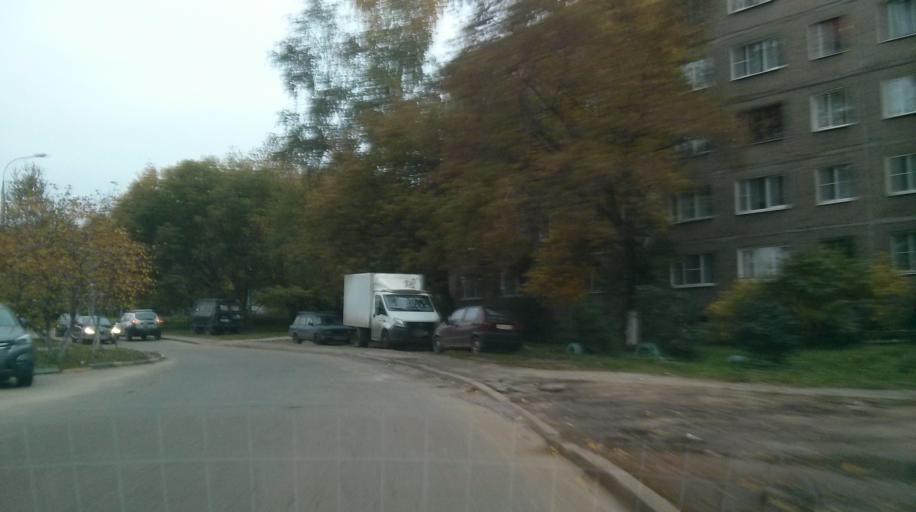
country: RU
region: Nizjnij Novgorod
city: Nizhniy Novgorod
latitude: 56.3041
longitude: 44.0448
